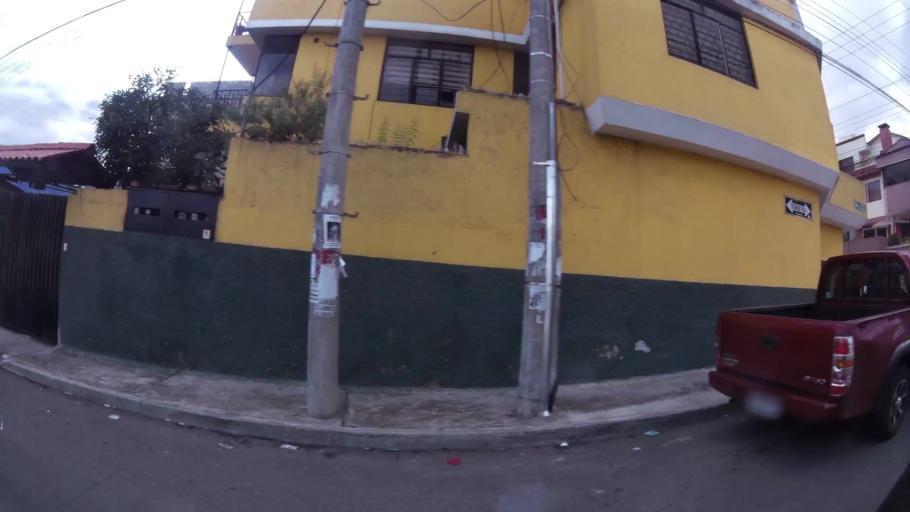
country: EC
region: Pichincha
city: Quito
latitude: -0.1355
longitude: -78.4642
